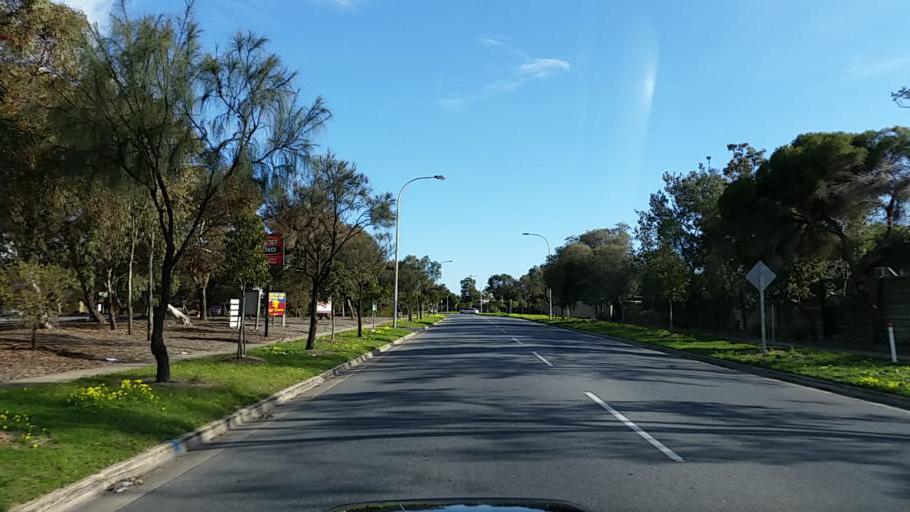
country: AU
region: South Australia
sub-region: Charles Sturt
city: West Lakes Shore
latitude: -34.8654
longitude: 138.4850
